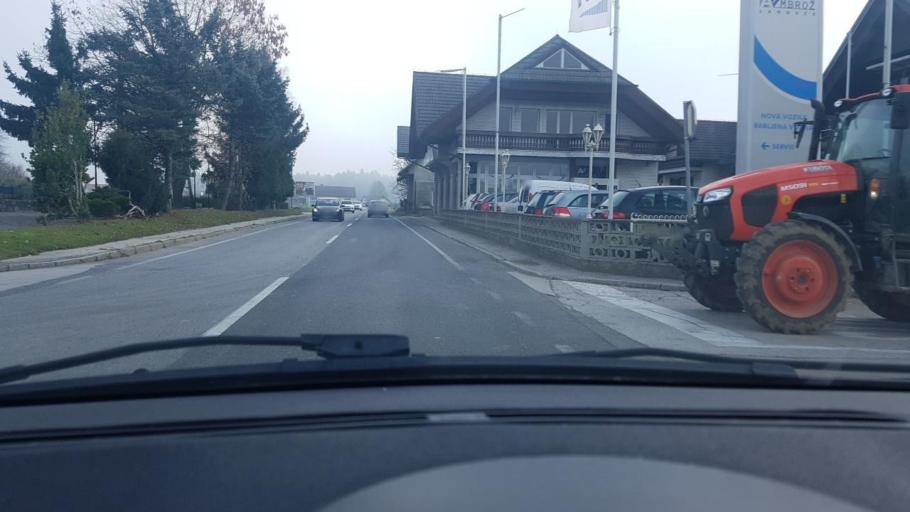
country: SI
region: Vodice
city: Vodice
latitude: 46.2184
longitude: 14.5012
